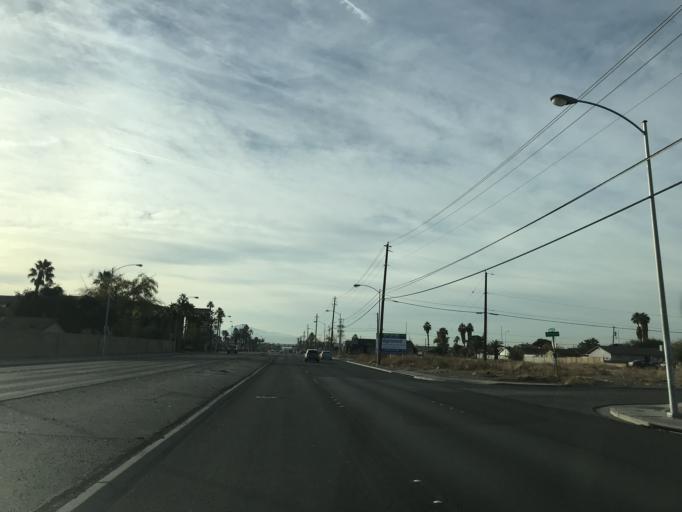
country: US
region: Nevada
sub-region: Clark County
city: Winchester
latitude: 36.1488
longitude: -115.0655
